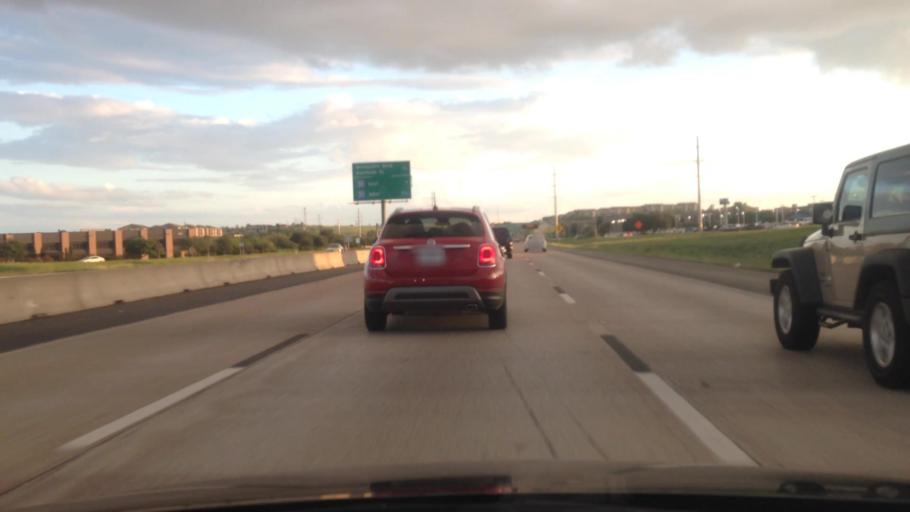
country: US
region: Texas
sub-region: Tarrant County
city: White Settlement
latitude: 32.7591
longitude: -97.4782
